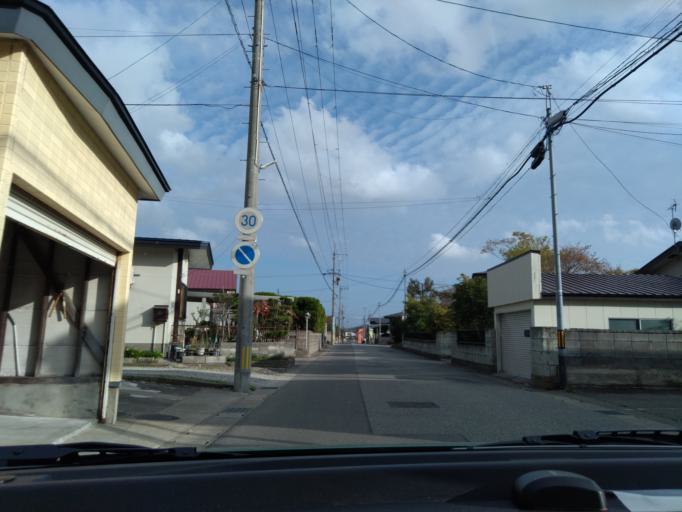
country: JP
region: Akita
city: Akita Shi
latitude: 39.7711
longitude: 140.0819
